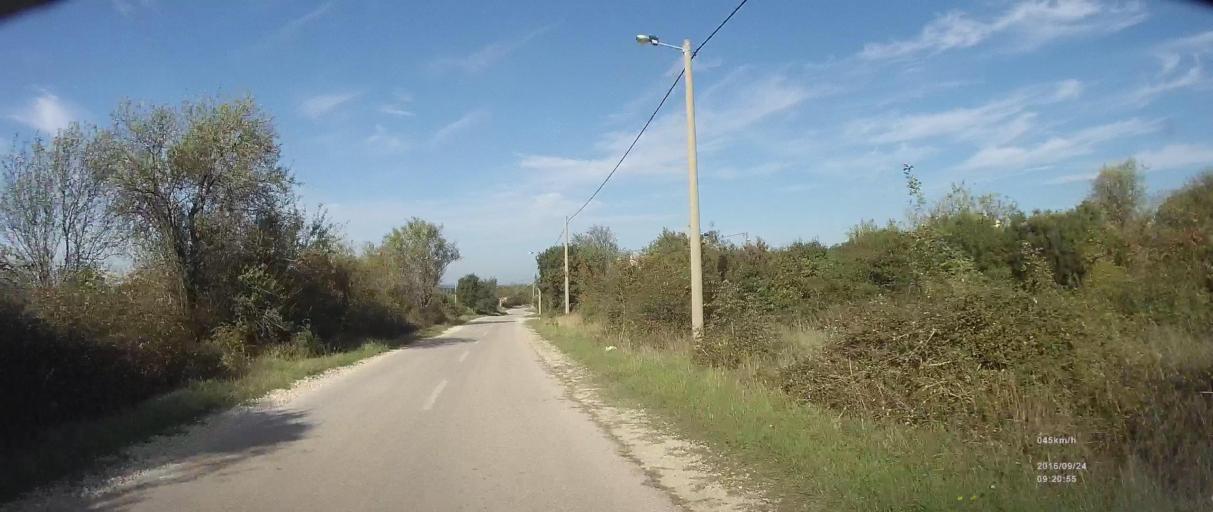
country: HR
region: Zadarska
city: Polaca
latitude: 44.0683
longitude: 15.4932
